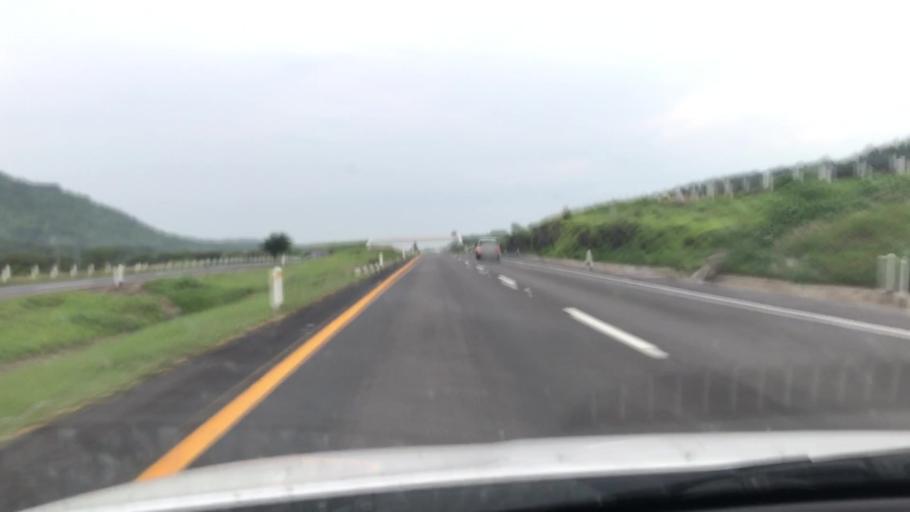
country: MX
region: Jalisco
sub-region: Zapotlan del Rey
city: Zapotlan del Rey
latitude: 20.5245
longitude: -102.9983
